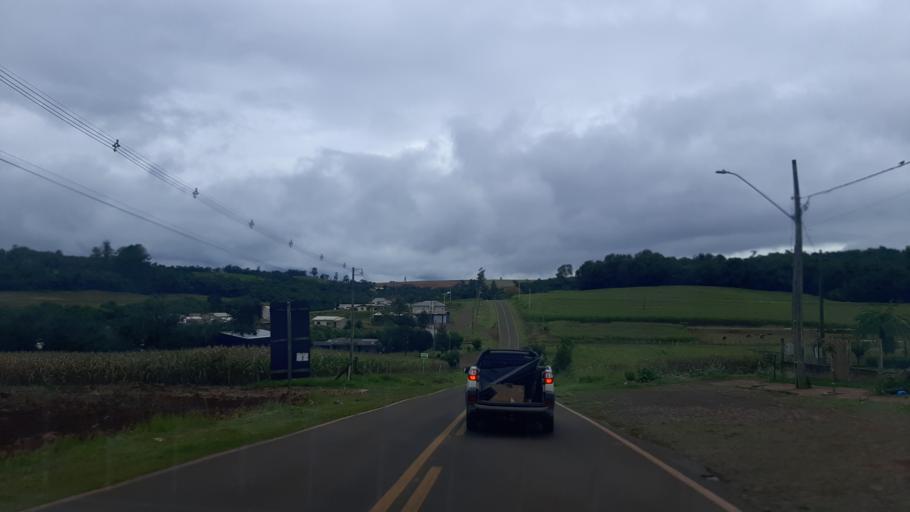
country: BR
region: Parana
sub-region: Ampere
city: Ampere
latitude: -25.9313
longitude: -53.4657
